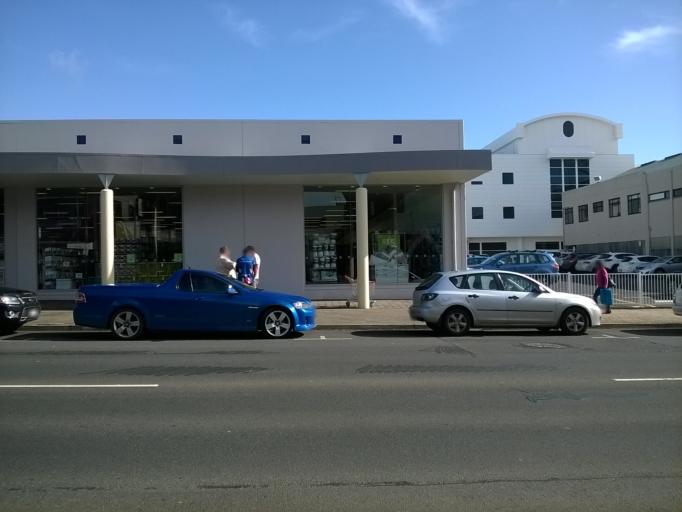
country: AU
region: Tasmania
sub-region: Burnie
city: Burnie
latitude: -41.0532
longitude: 145.9049
